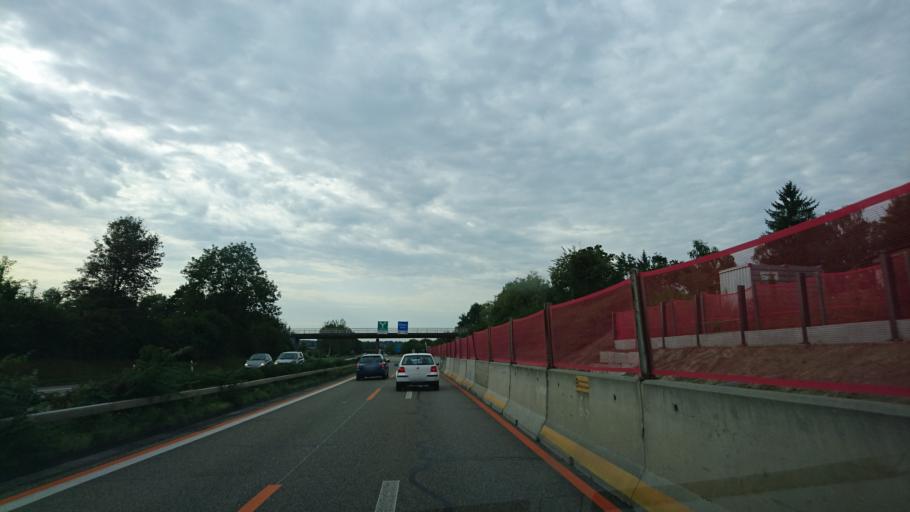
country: CH
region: Zurich
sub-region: Bezirk Uster
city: Wangen
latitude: 47.4043
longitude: 8.6476
